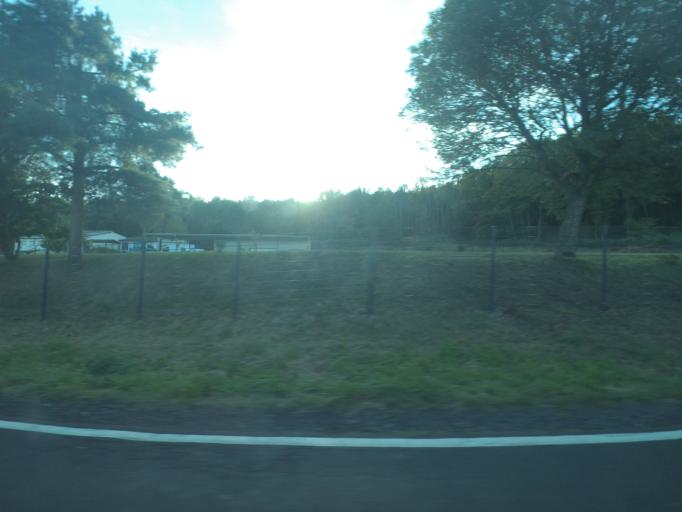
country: DE
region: Hesse
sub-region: Regierungsbezirk Darmstadt
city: Birstein
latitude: 50.3159
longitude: 9.2850
